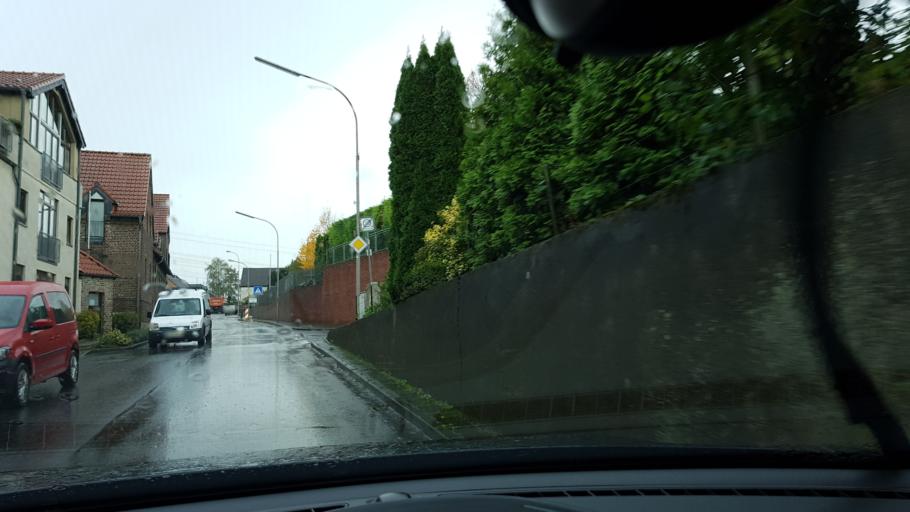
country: DE
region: North Rhine-Westphalia
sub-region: Regierungsbezirk Dusseldorf
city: Rommerskirchen
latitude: 51.0614
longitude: 6.7166
